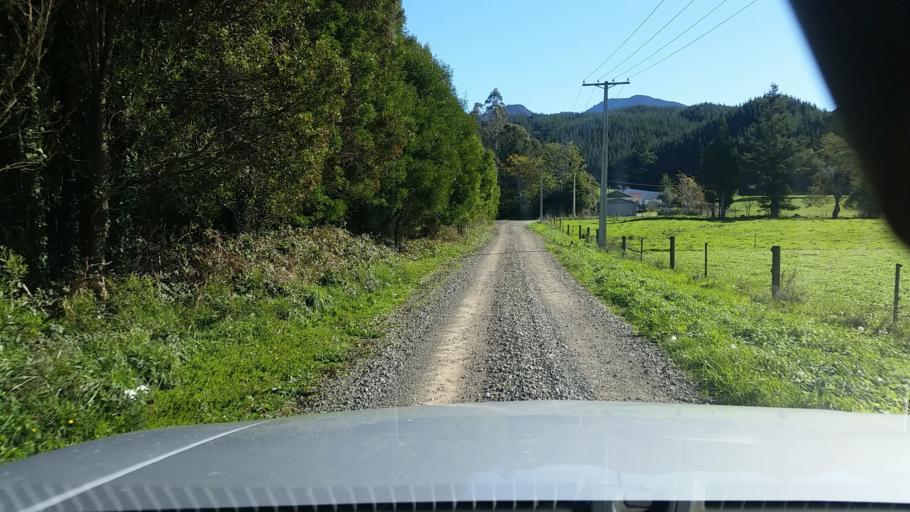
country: NZ
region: Nelson
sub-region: Nelson City
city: Nelson
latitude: -41.2379
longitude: 173.5739
